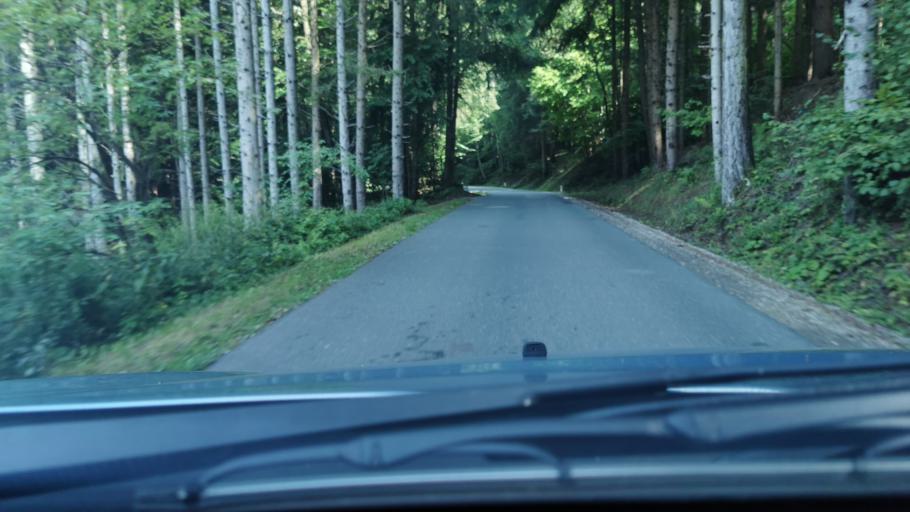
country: AT
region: Styria
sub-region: Politischer Bezirk Weiz
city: Baierdorf-Umgebung
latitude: 47.3092
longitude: 15.7065
